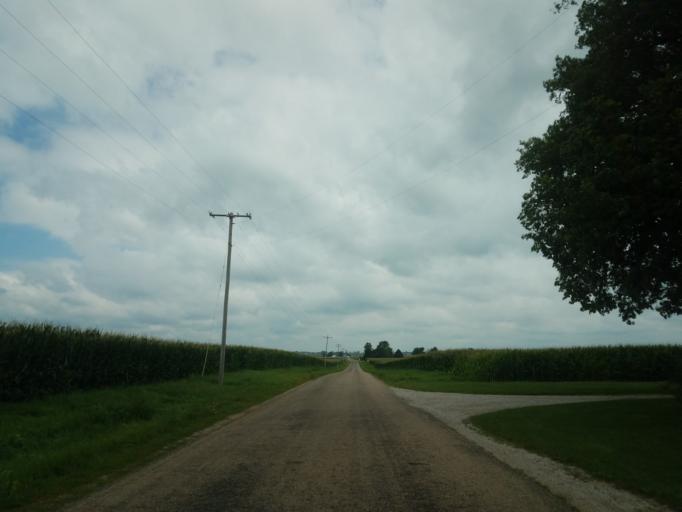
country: US
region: Illinois
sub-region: McLean County
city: Twin Grove
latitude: 40.4253
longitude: -89.0622
